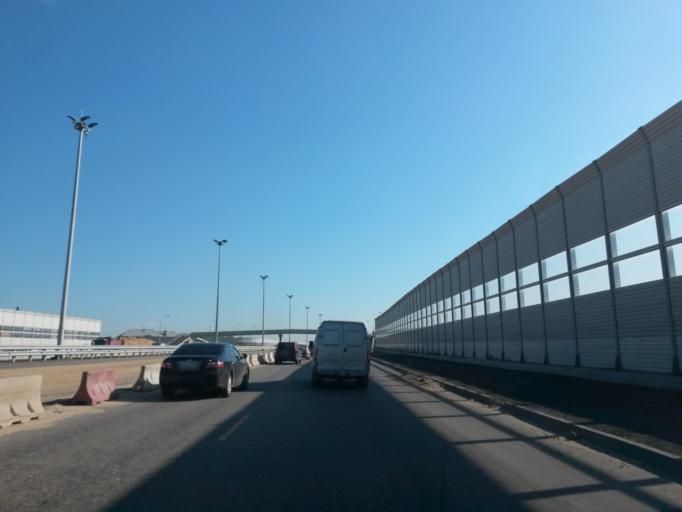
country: RU
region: Moskovskaya
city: Lesnyye Polyany
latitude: 55.9688
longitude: 37.8445
